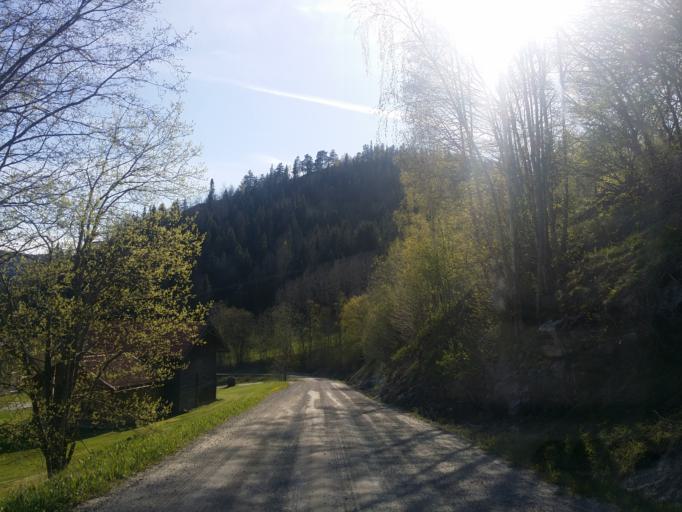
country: NO
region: Telemark
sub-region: Seljord
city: Seljord
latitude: 59.6145
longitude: 8.6921
